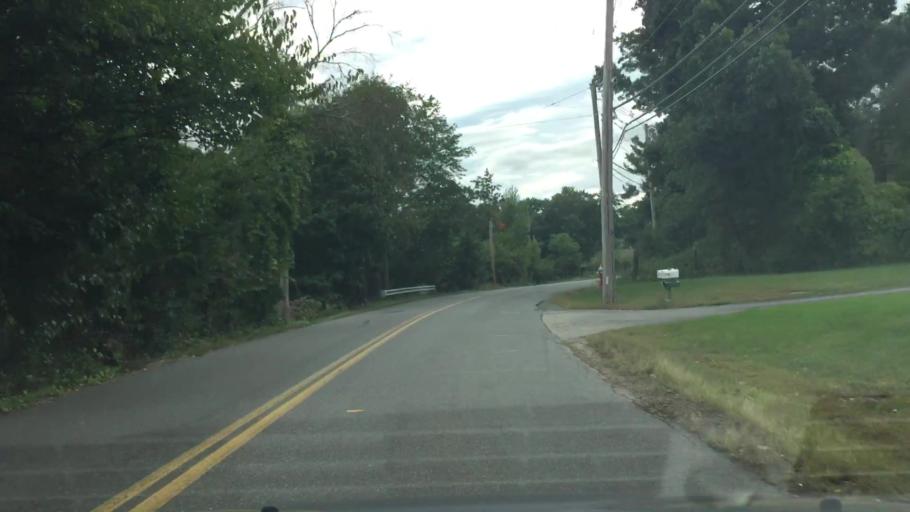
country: US
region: Massachusetts
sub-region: Middlesex County
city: Lowell
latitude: 42.6664
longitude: -71.3470
